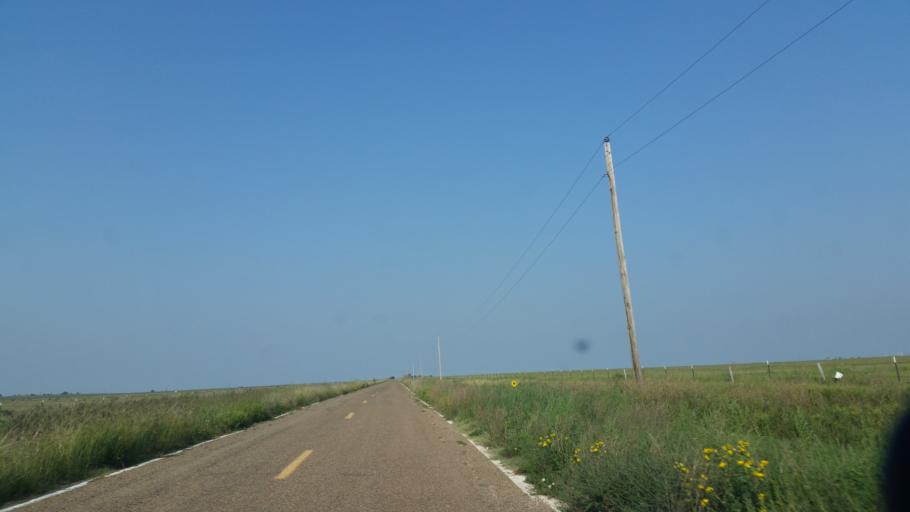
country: US
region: New Mexico
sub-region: Quay County
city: Logan
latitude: 34.9234
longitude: -103.3190
